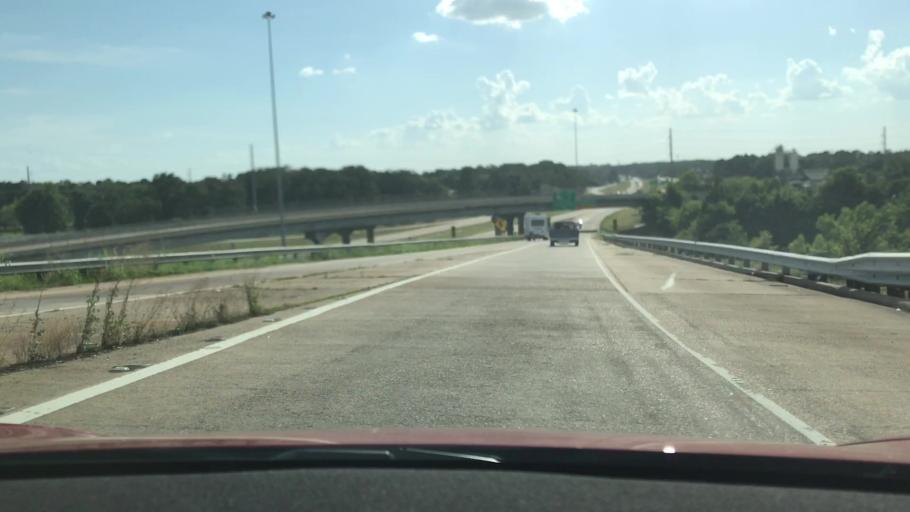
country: US
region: Louisiana
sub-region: Bossier Parish
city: Bossier City
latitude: 32.4202
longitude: -93.7523
